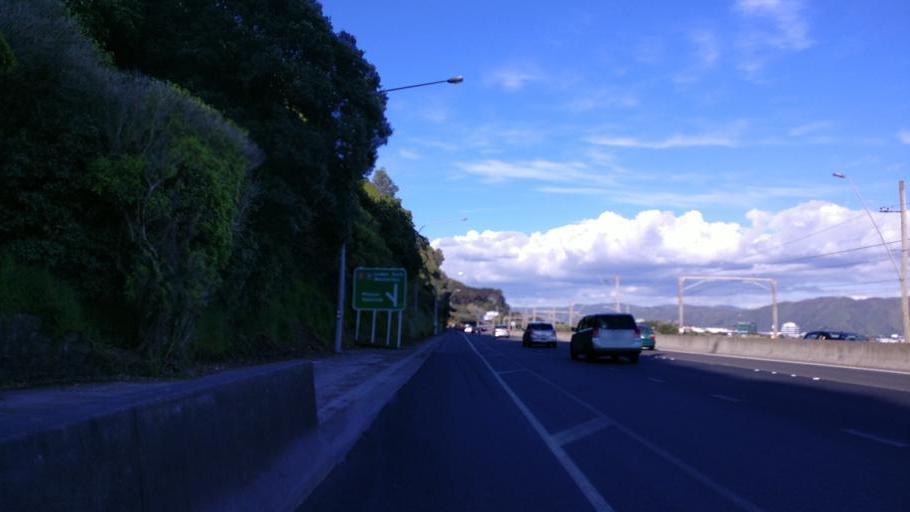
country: NZ
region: Wellington
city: Petone
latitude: -41.2253
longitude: 174.8539
